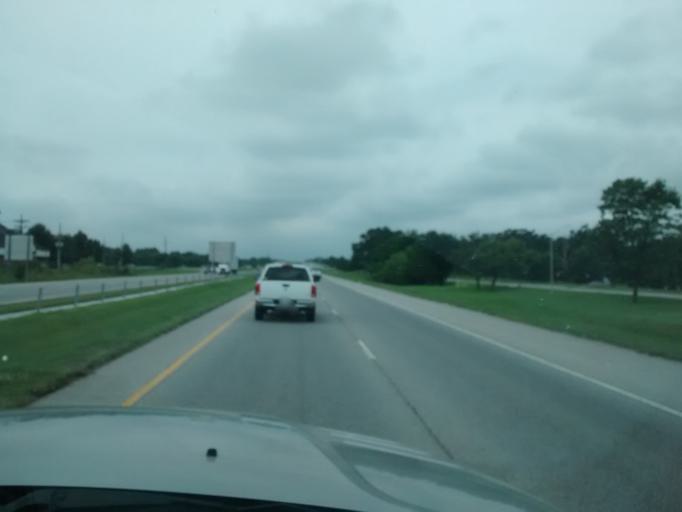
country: US
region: Arkansas
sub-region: Washington County
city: Johnson
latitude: 36.1143
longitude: -94.1549
